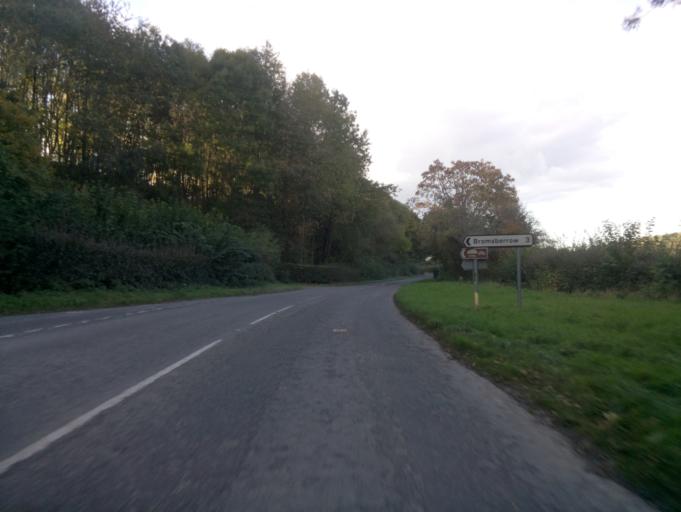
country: GB
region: England
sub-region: Herefordshire
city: Ledbury
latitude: 52.0352
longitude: -2.3932
